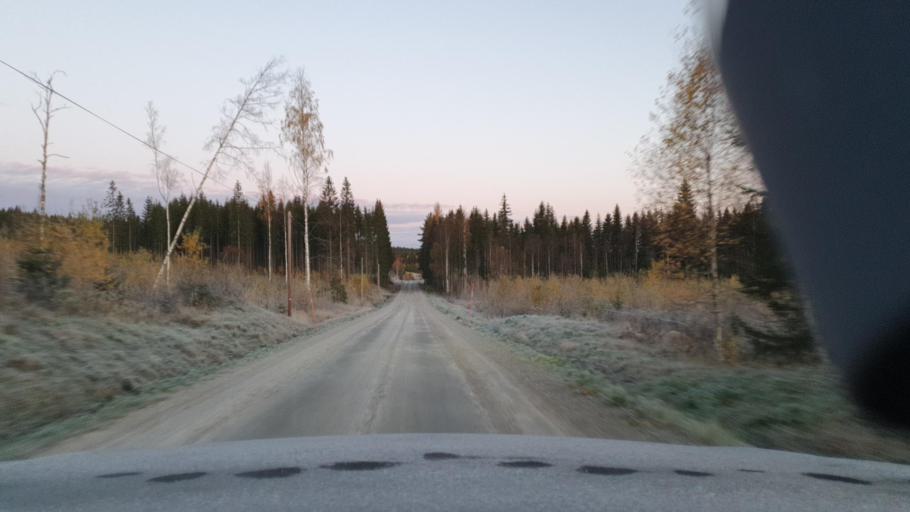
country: SE
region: Vaermland
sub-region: Arvika Kommun
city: Arvika
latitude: 59.7906
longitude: 12.7572
